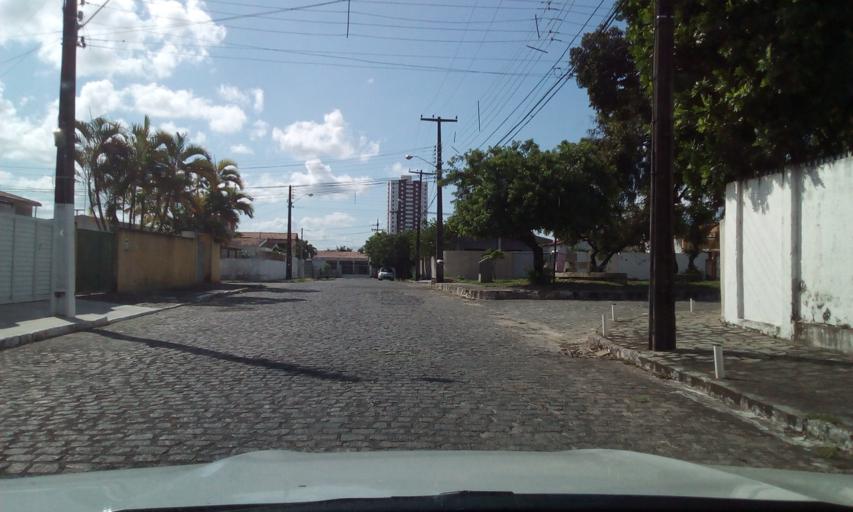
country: BR
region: Paraiba
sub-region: Joao Pessoa
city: Joao Pessoa
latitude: -7.1127
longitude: -34.8634
